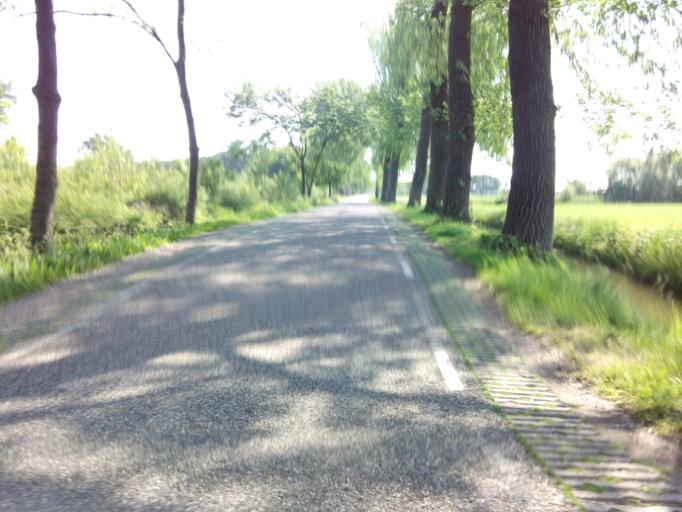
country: NL
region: Utrecht
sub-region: Gemeente Wijk bij Duurstede
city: Wijk bij Duurstede
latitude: 51.9850
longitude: 5.3680
